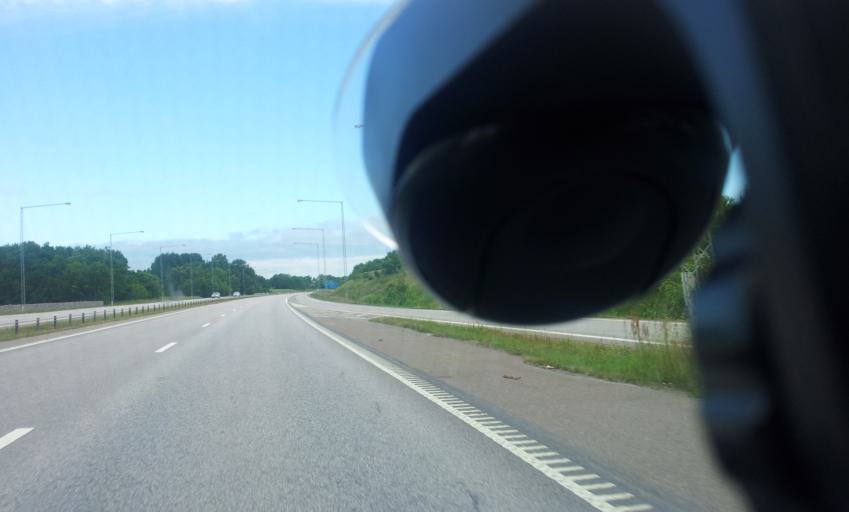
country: SE
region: Kalmar
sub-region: Kalmar Kommun
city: Lindsdal
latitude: 56.6953
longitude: 16.3151
